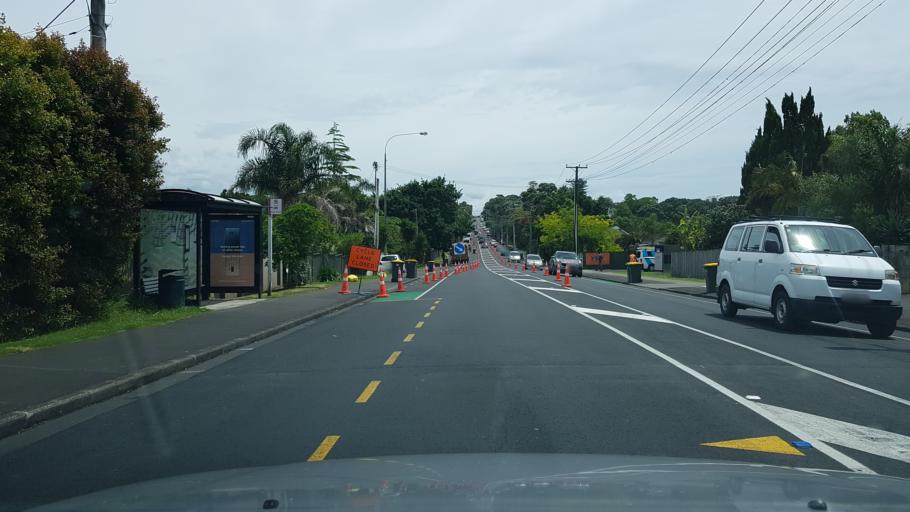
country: NZ
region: Auckland
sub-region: Auckland
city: North Shore
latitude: -36.8047
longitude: 174.7884
